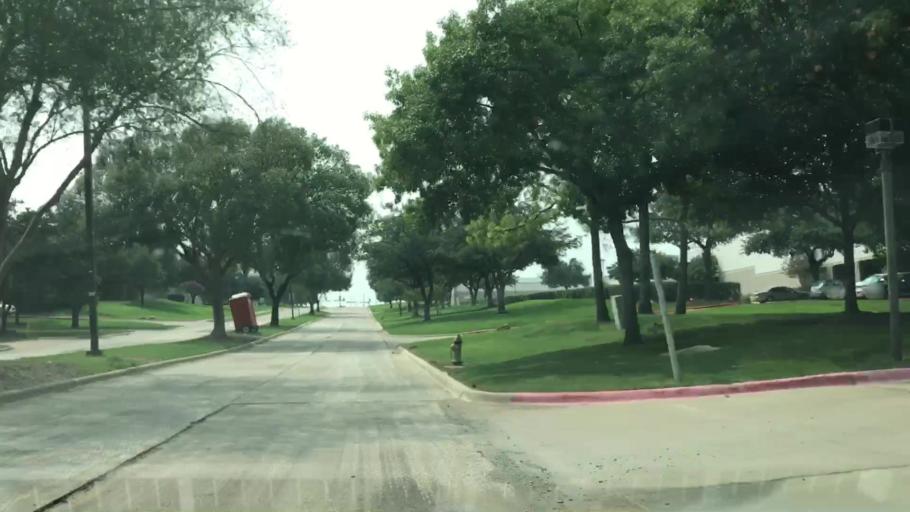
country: US
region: Texas
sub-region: Dallas County
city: Irving
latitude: 32.8715
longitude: -96.9872
